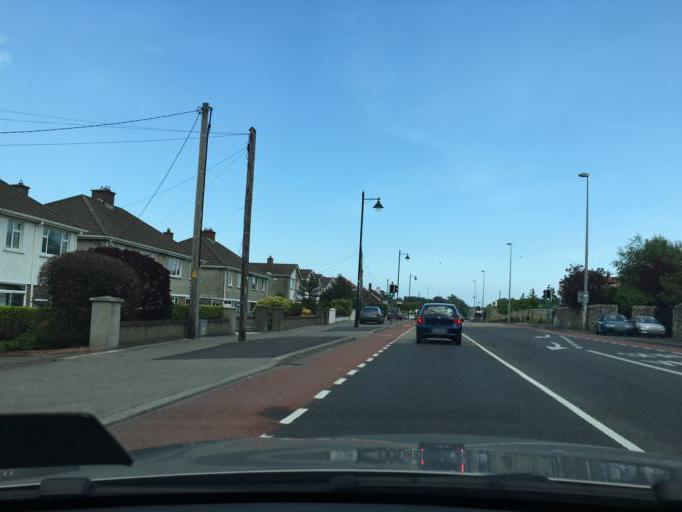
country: IE
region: Leinster
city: Templeogue
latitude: 53.2817
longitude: -6.2930
